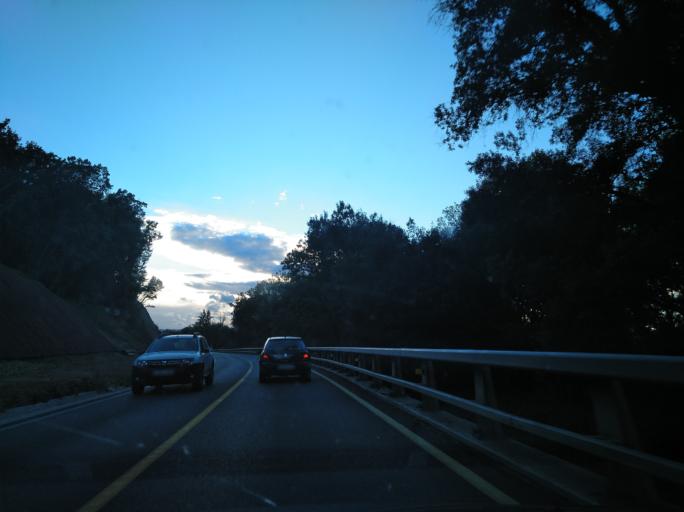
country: ES
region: Catalonia
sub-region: Provincia de Girona
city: Bescano
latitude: 41.9708
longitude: 2.7546
